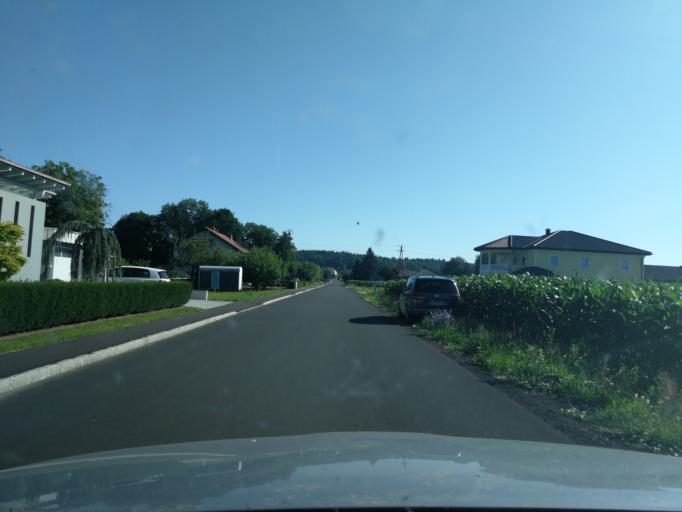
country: AT
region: Burgenland
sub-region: Politischer Bezirk Jennersdorf
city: Konigsdorf
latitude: 47.0078
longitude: 16.1737
